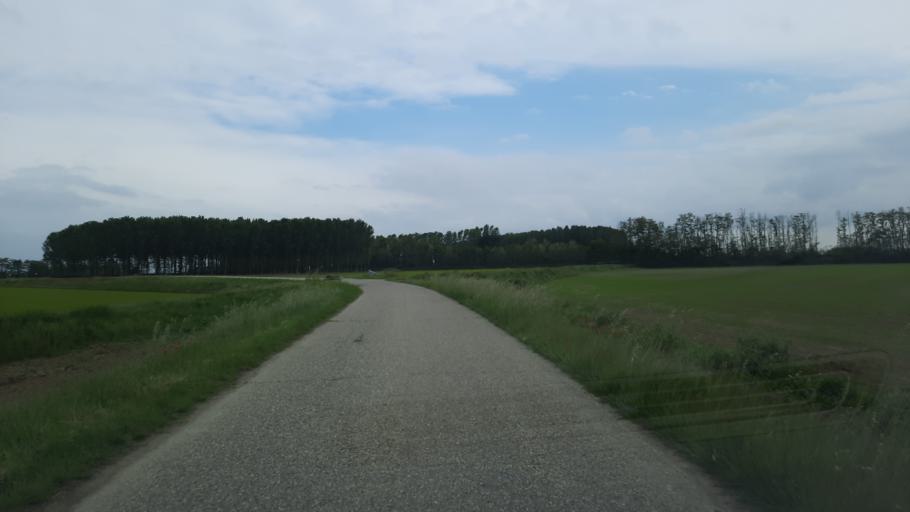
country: IT
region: Lombardy
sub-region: Provincia di Pavia
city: Cozzo
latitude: 45.2221
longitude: 8.6050
